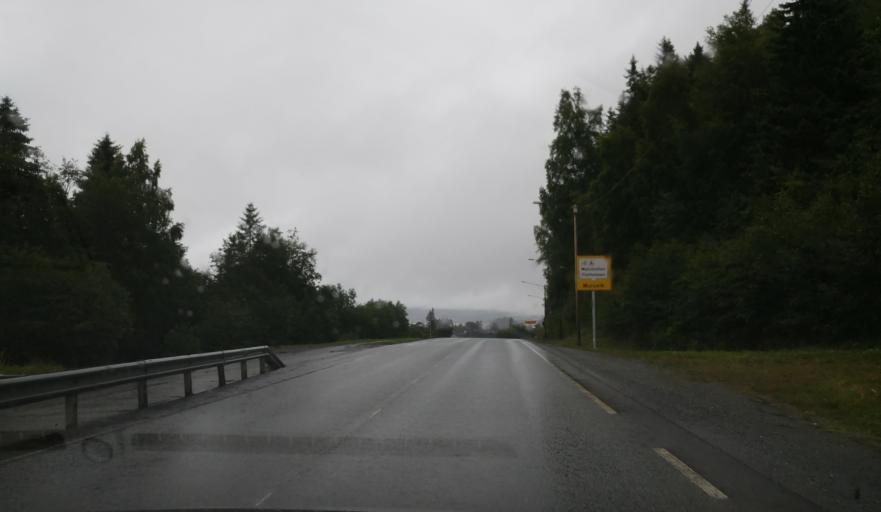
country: NO
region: Sor-Trondelag
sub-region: Malvik
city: Hommelvik
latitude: 63.4301
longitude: 10.8295
